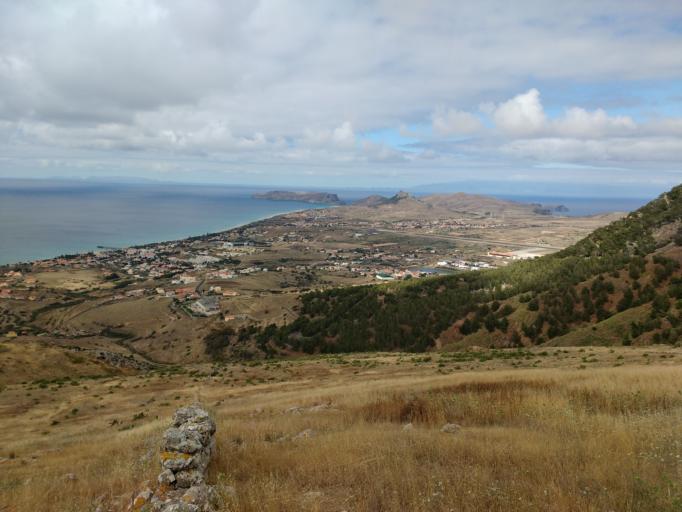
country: PT
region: Madeira
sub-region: Porto Santo
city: Camacha
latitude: 33.0815
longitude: -16.3263
